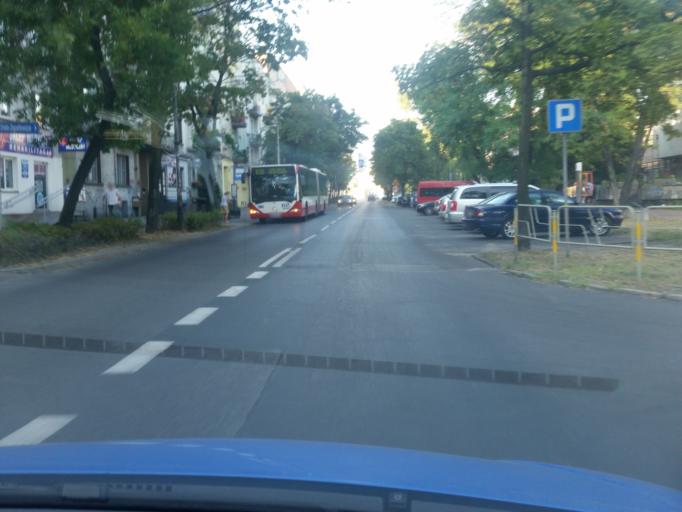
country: PL
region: Silesian Voivodeship
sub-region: Sosnowiec
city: Sosnowiec
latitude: 50.2719
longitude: 19.1287
